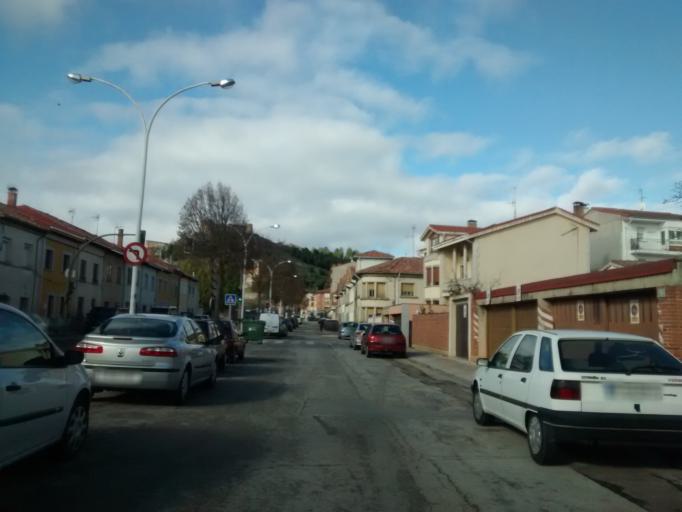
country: ES
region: Castille and Leon
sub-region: Provincia de Palencia
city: Aguilar de Campoo
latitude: 42.7942
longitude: -4.2577
